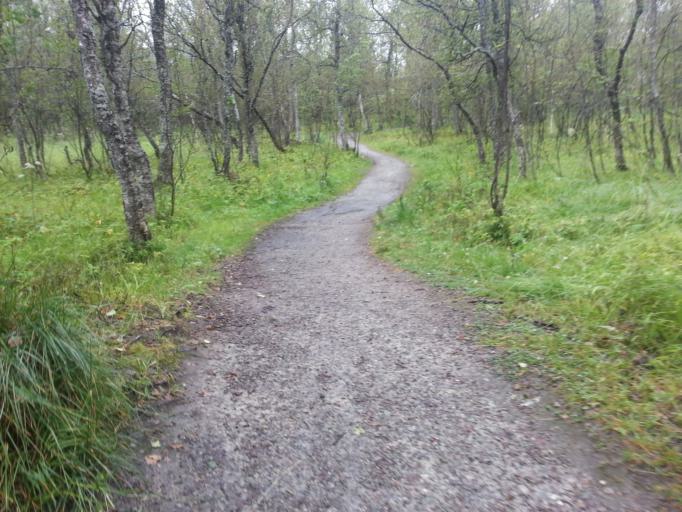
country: NO
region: Troms
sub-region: Tromso
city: Tromso
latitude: 69.6779
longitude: 18.9716
